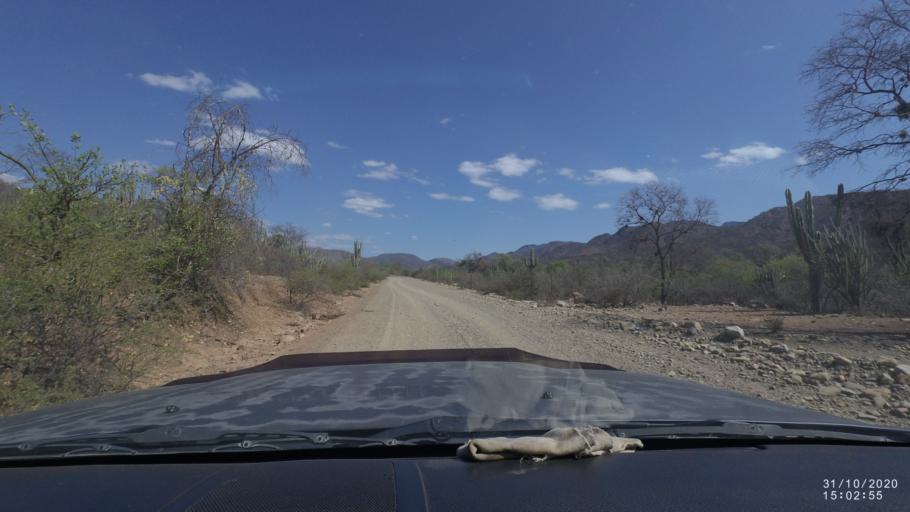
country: BO
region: Cochabamba
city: Aiquile
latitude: -18.2724
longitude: -64.8098
